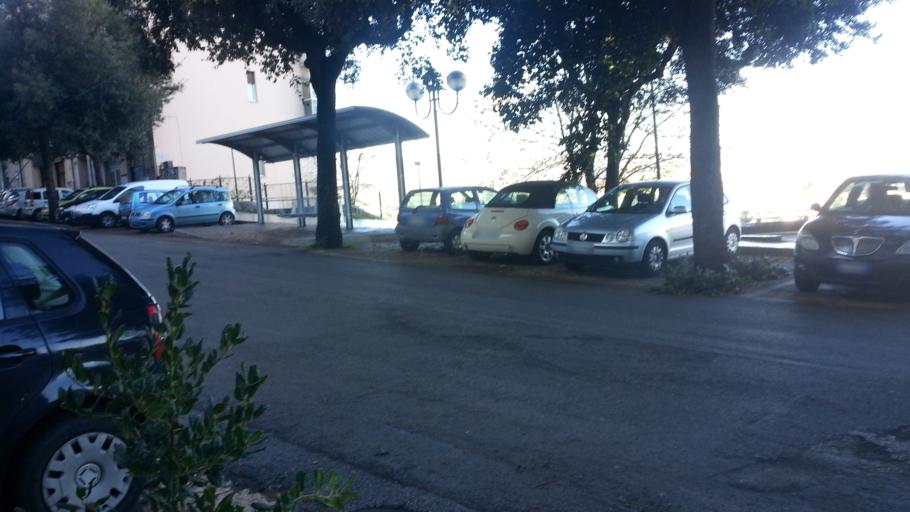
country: IT
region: Basilicate
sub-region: Provincia di Potenza
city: Potenza
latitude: 40.6396
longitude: 15.8039
